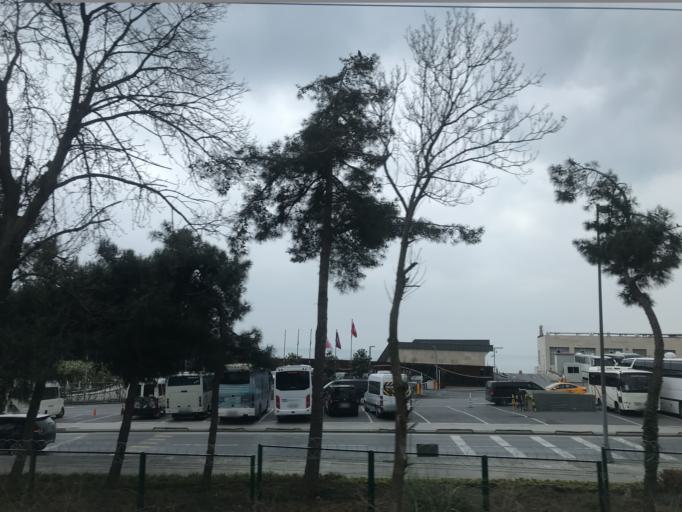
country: TR
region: Istanbul
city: Bahcelievler
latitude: 40.9646
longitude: 28.8012
